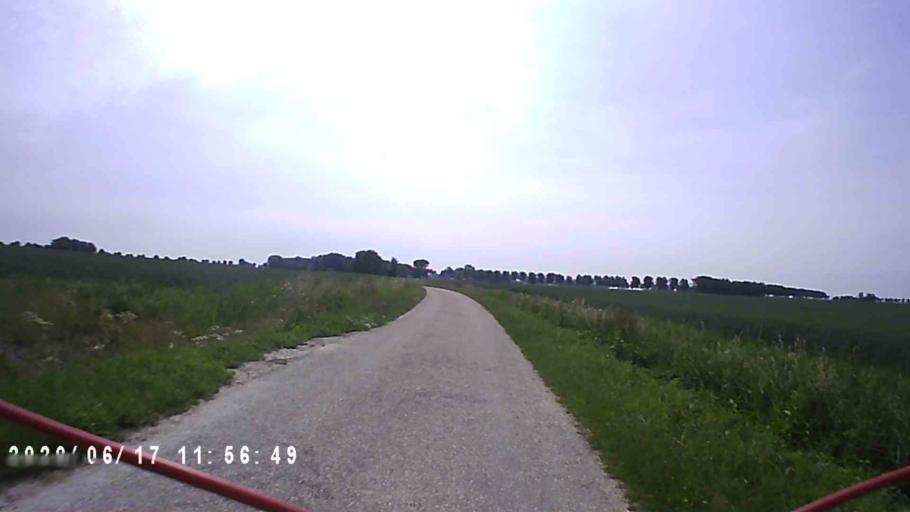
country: NL
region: Groningen
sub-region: Gemeente De Marne
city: Ulrum
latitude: 53.3482
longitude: 6.3217
